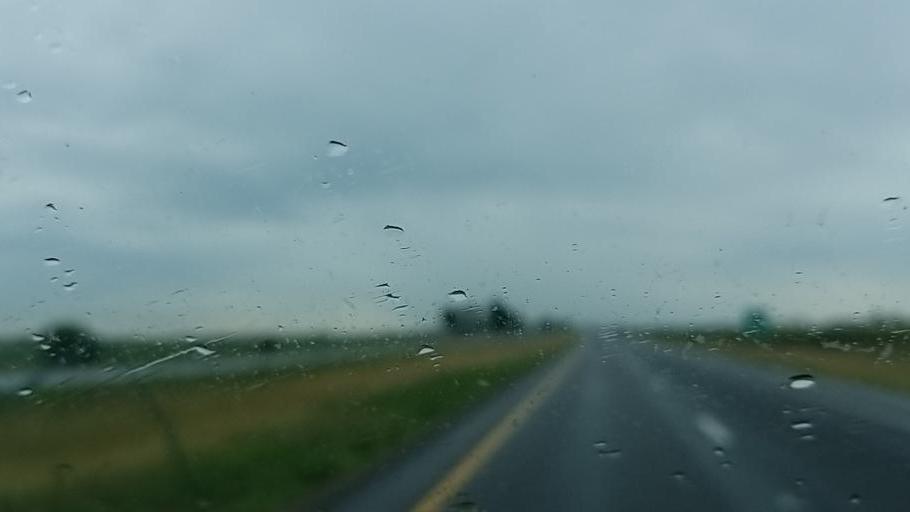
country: US
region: Ohio
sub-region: Van Wert County
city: Convoy
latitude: 40.9581
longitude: -84.7347
